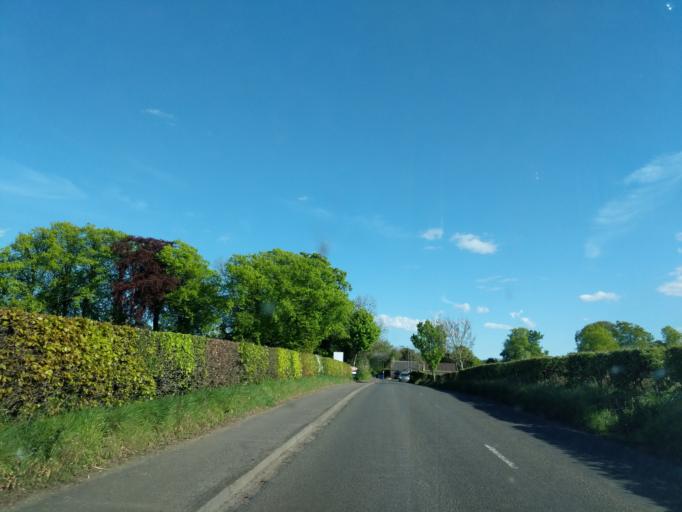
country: GB
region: Scotland
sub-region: Edinburgh
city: Ratho
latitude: 55.9095
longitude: -3.3703
